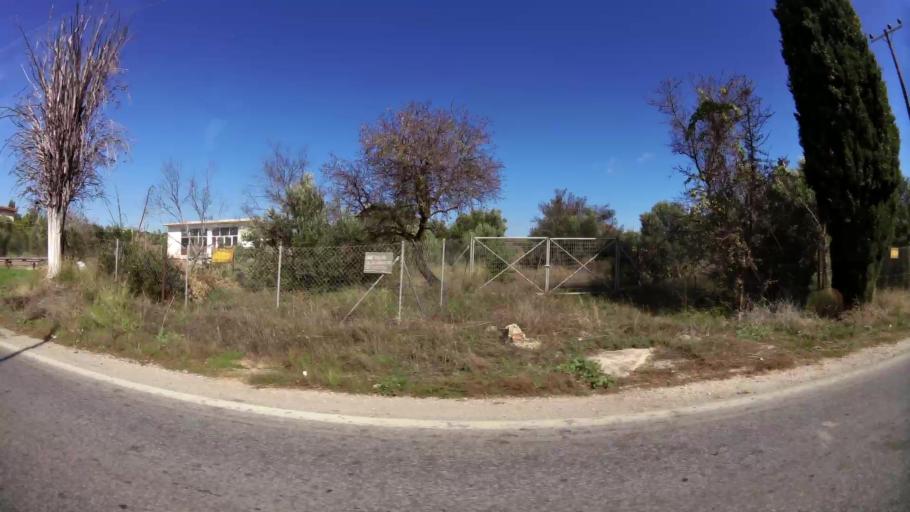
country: GR
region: Attica
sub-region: Nomarchia Anatolikis Attikis
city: Koropi
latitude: 37.8883
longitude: 23.8952
